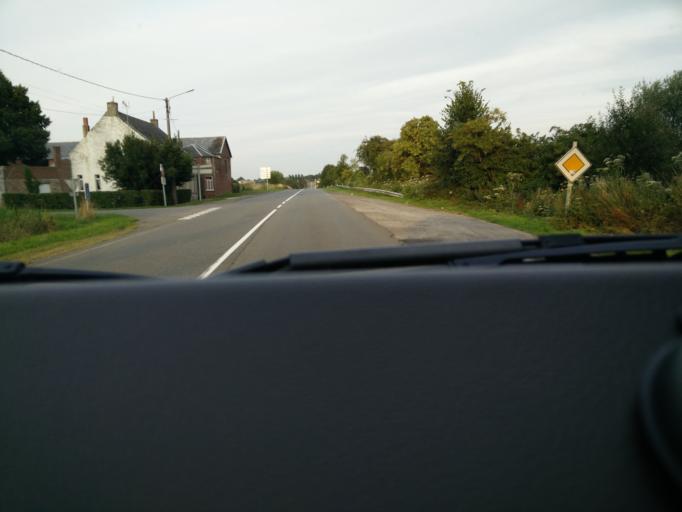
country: FR
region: Nord-Pas-de-Calais
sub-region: Departement du Nord
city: Bavay
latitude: 50.3025
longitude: 3.7710
